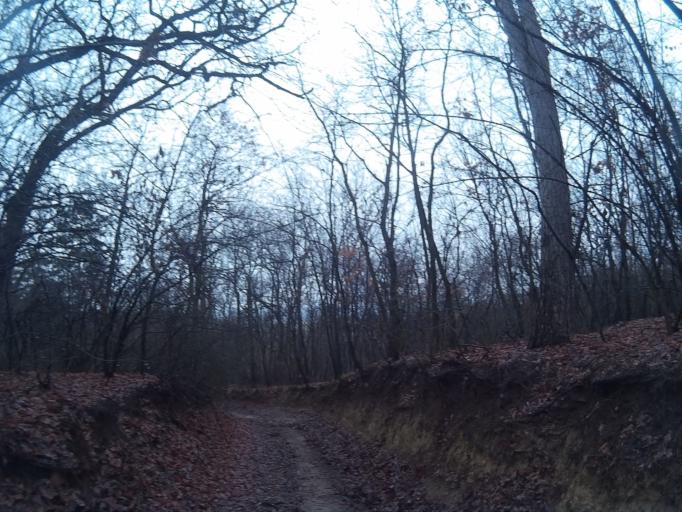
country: HU
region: Komarom-Esztergom
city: Tat
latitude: 47.7264
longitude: 18.6084
